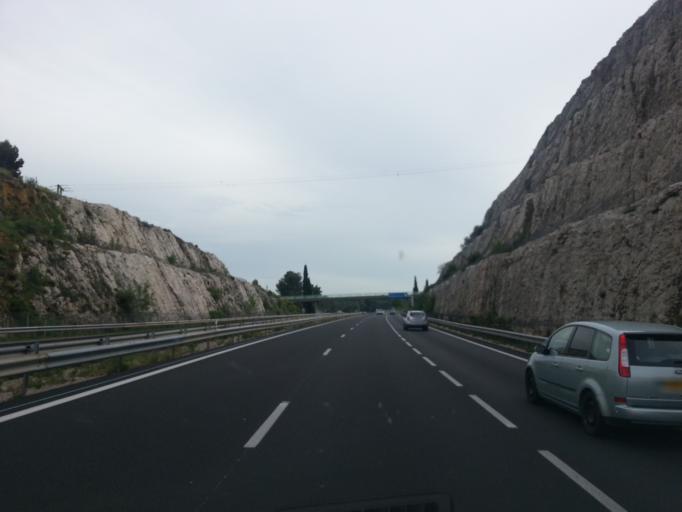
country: FR
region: Languedoc-Roussillon
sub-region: Departement du Gard
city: Roquemaure
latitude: 44.0535
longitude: 4.7669
